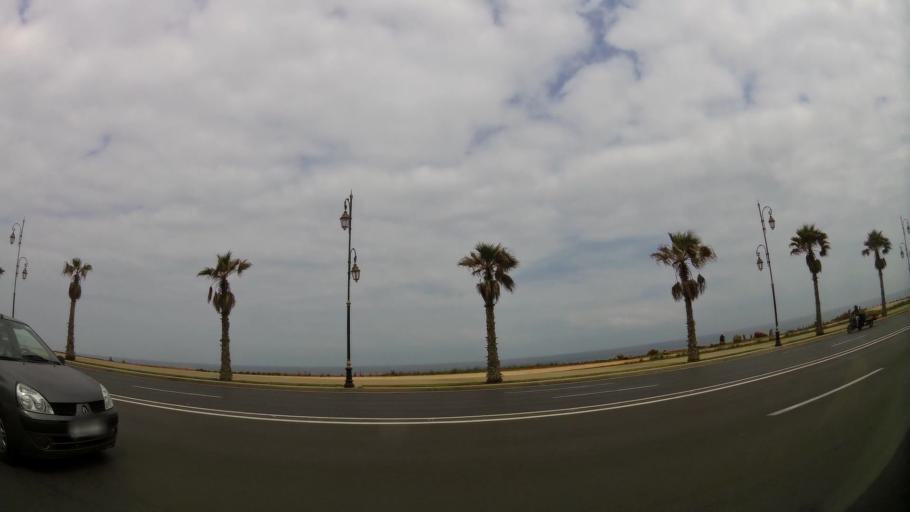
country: MA
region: Rabat-Sale-Zemmour-Zaer
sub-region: Rabat
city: Rabat
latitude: 33.9940
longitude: -6.8812
